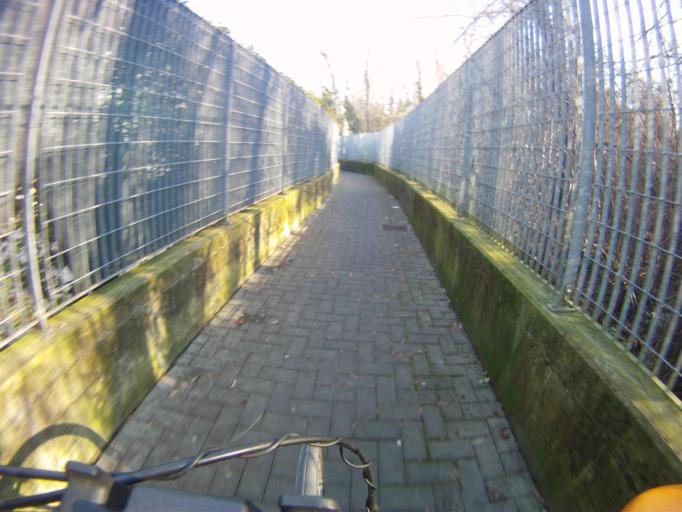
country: IT
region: Veneto
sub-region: Provincia di Padova
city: Piove di Sacco-Piovega
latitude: 45.2953
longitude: 12.0308
